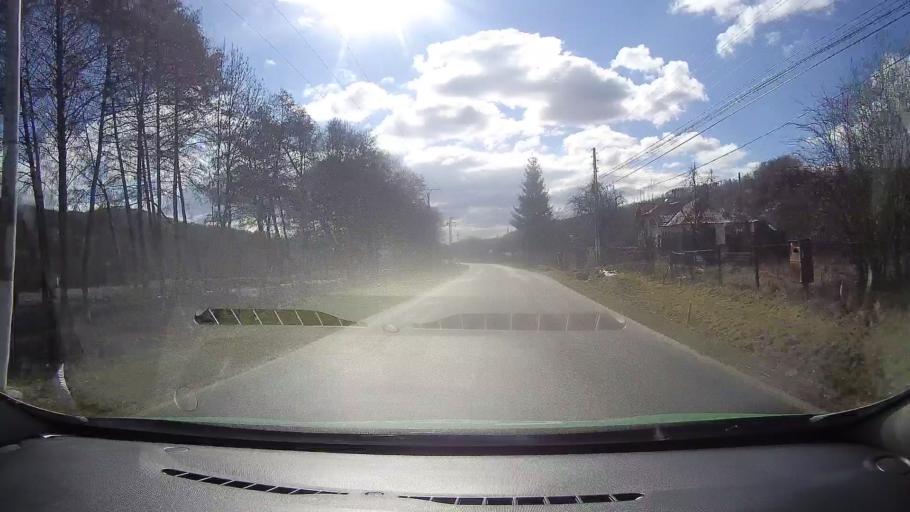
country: RO
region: Dambovita
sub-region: Comuna Runcu
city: Badeni
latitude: 45.1626
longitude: 25.3965
